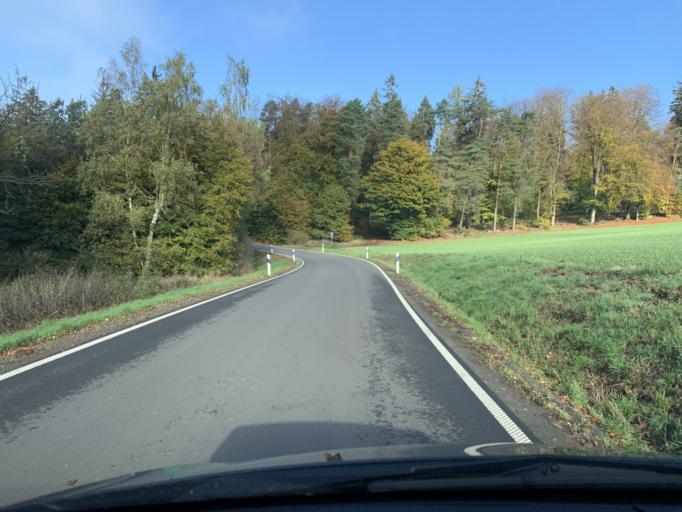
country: DE
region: Hesse
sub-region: Regierungsbezirk Kassel
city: Ottrau
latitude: 50.7268
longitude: 9.3973
